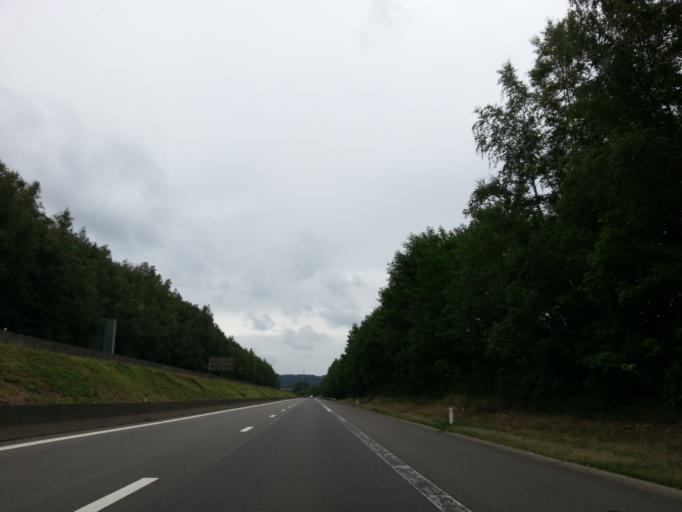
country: BE
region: Wallonia
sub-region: Province de Liege
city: Malmedy
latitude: 50.3763
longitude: 6.0112
